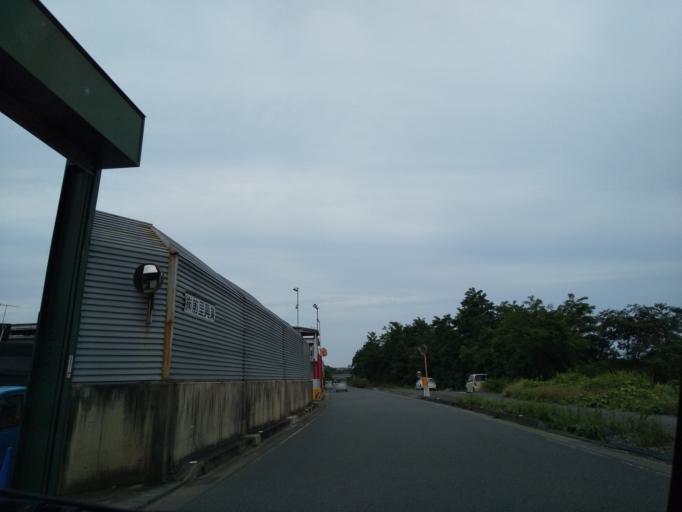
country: JP
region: Kanagawa
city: Zama
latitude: 35.4885
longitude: 139.3535
